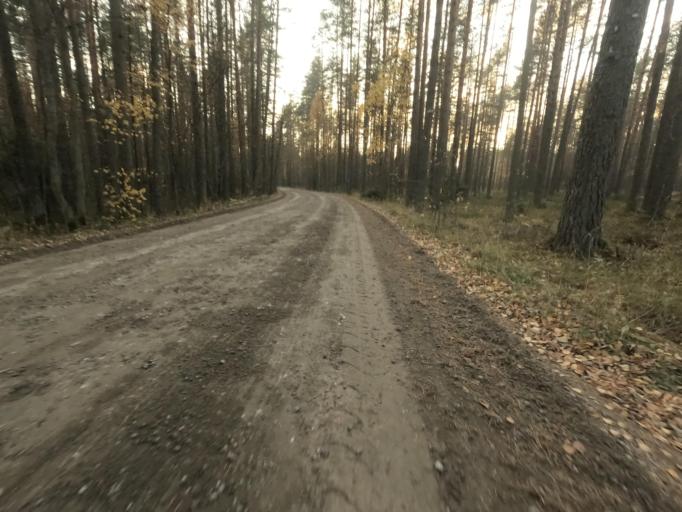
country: RU
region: St.-Petersburg
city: Repino
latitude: 60.1902
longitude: 29.8833
